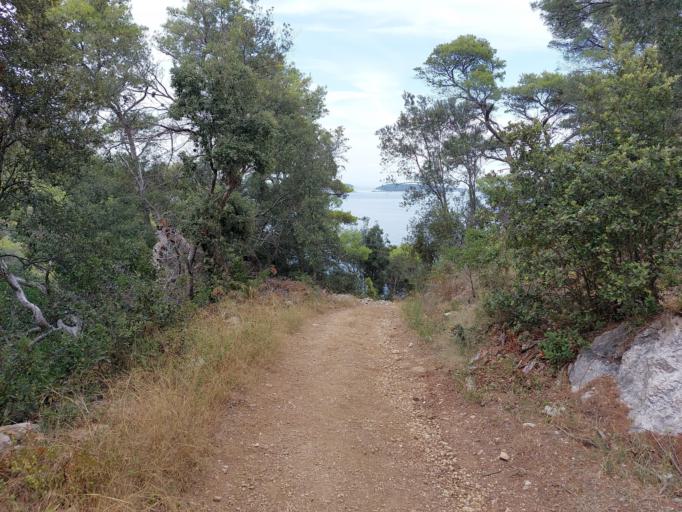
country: HR
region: Dubrovacko-Neretvanska
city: Smokvica
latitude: 42.7617
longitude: 16.9358
